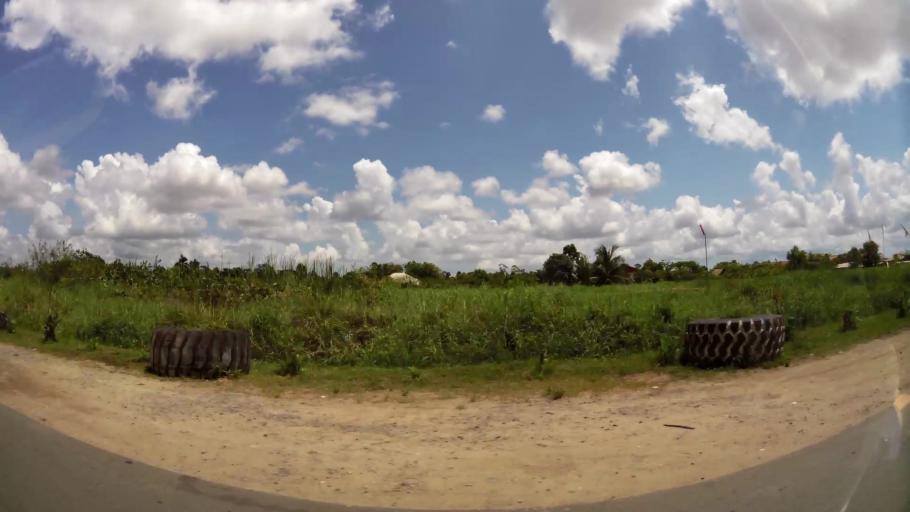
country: SR
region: Paramaribo
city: Paramaribo
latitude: 5.8075
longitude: -55.1555
